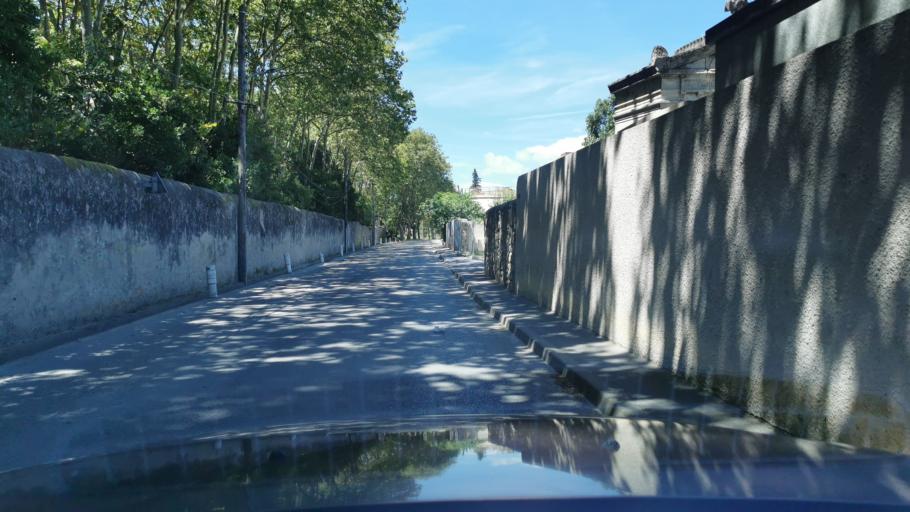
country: FR
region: Languedoc-Roussillon
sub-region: Departement de l'Aude
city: Armissan
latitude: 43.1876
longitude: 3.0942
